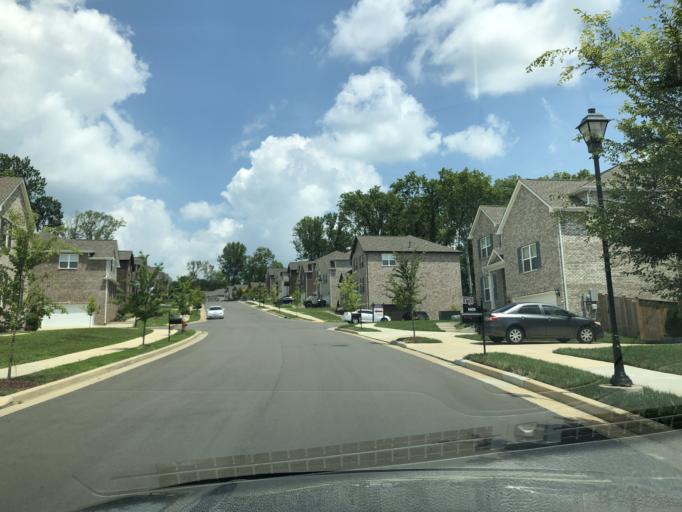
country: US
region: Tennessee
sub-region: Williamson County
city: Nolensville
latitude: 36.0176
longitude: -86.6919
